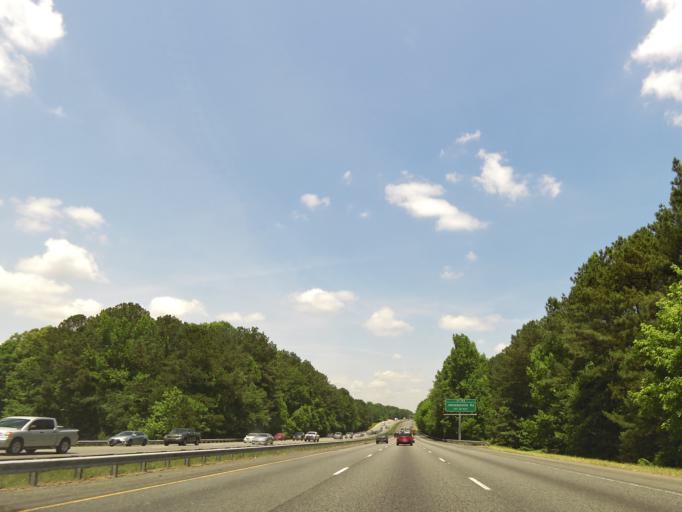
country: US
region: Georgia
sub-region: Monroe County
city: Forsyth
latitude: 33.1013
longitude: -84.0001
